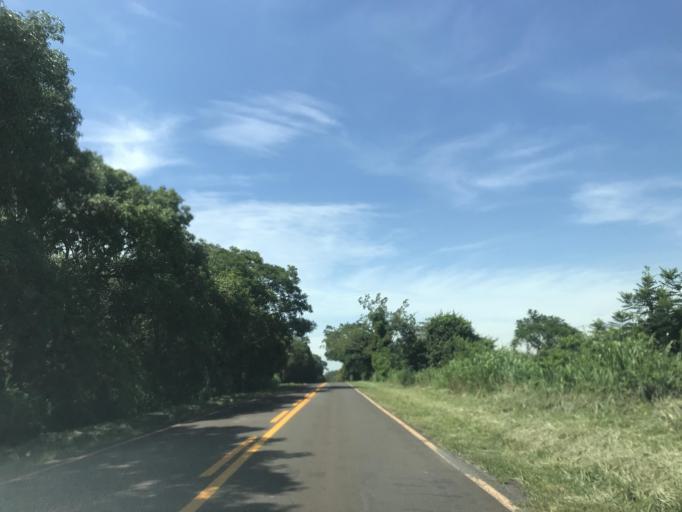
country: BR
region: Parana
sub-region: Terra Rica
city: Terra Rica
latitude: -22.7859
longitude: -52.6561
